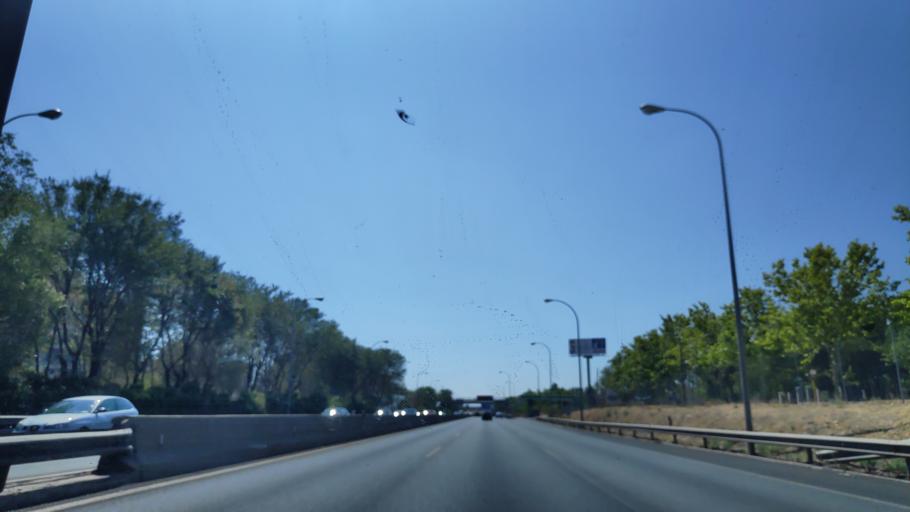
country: ES
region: Madrid
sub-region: Provincia de Madrid
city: Getafe
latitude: 40.3049
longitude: -3.7395
